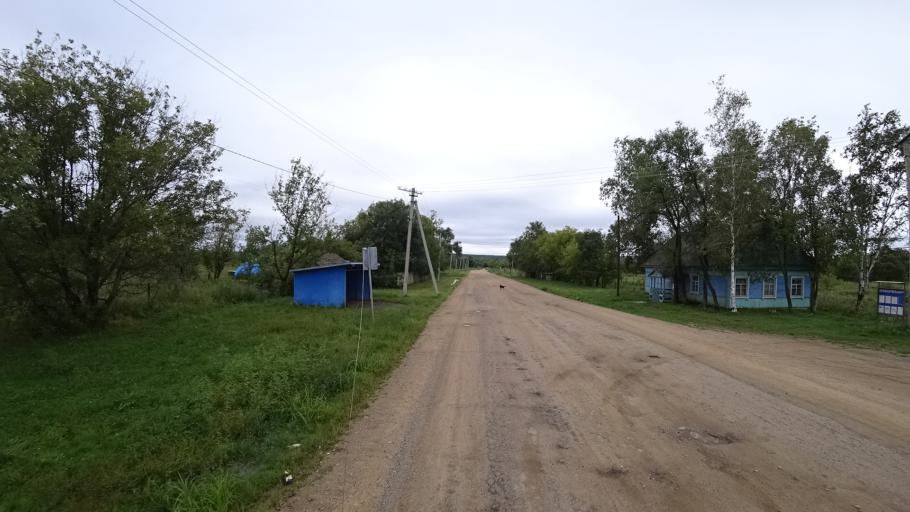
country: RU
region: Primorskiy
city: Rettikhovka
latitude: 44.1380
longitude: 132.6469
